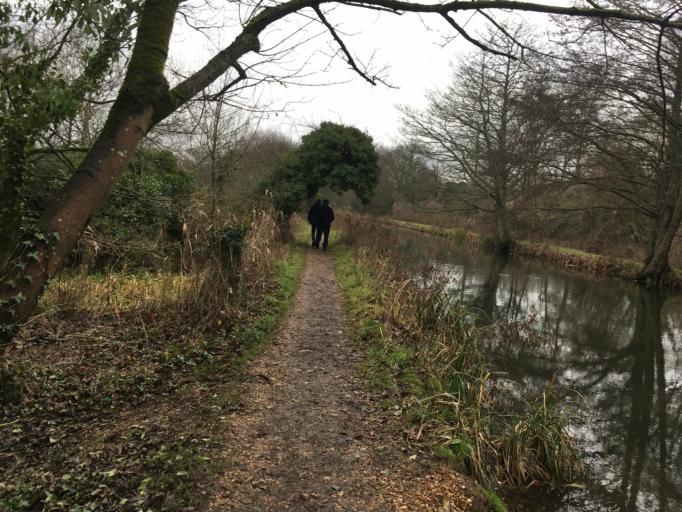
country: GB
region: England
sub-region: Hampshire
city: Compton
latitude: 50.9939
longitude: -1.3402
